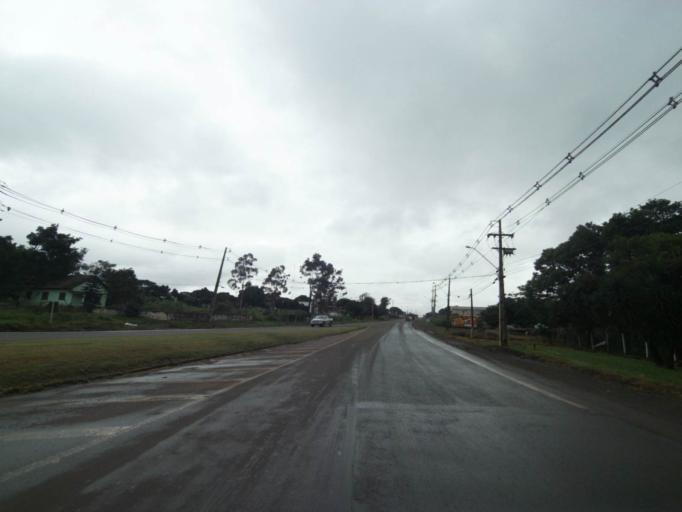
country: BR
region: Parana
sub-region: Marechal Candido Rondon
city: Marechal Candido Rondon
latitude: -24.5685
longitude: -54.0337
